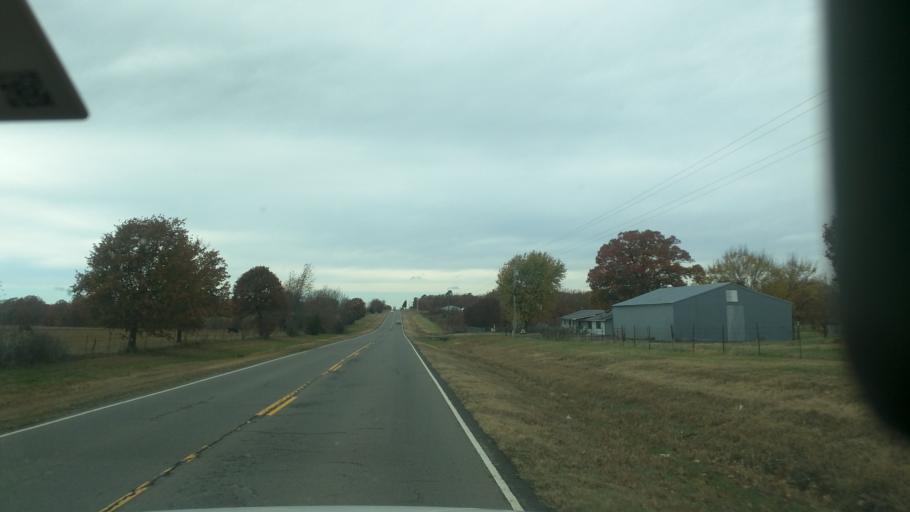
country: US
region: Oklahoma
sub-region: Cherokee County
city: Park Hill
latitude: 35.8976
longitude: -94.7925
